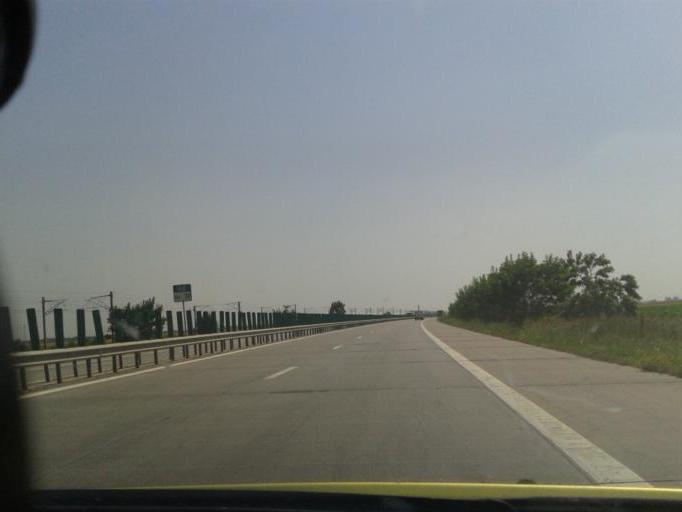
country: RO
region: Calarasi
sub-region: Comuna Belciugatele
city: Belciugatele
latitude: 44.4554
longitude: 26.4593
